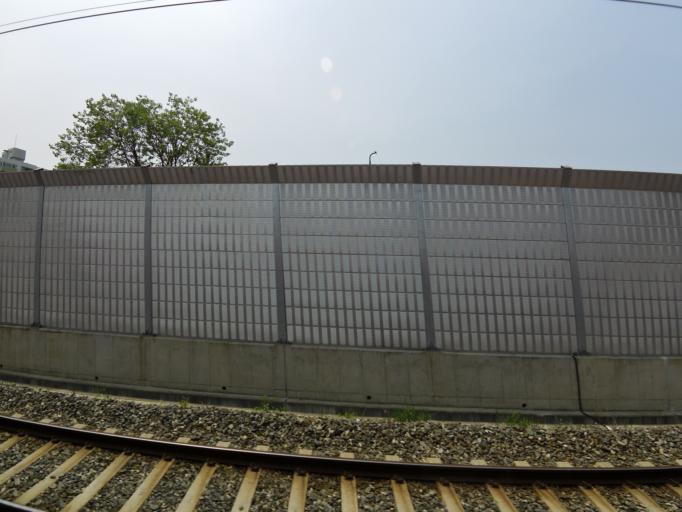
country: KR
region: Daejeon
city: Daejeon
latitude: 36.3214
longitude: 127.4397
